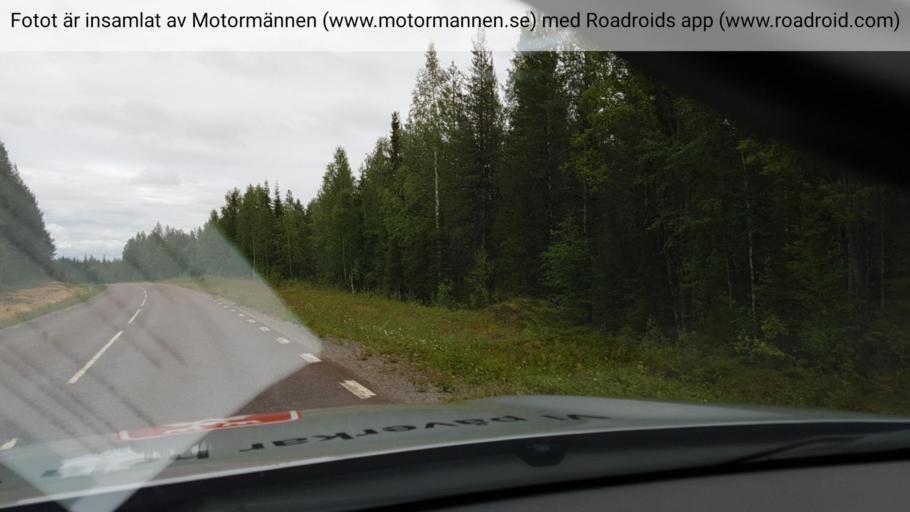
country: SE
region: Norrbotten
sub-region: Overkalix Kommun
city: OEverkalix
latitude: 67.0660
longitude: 22.4045
